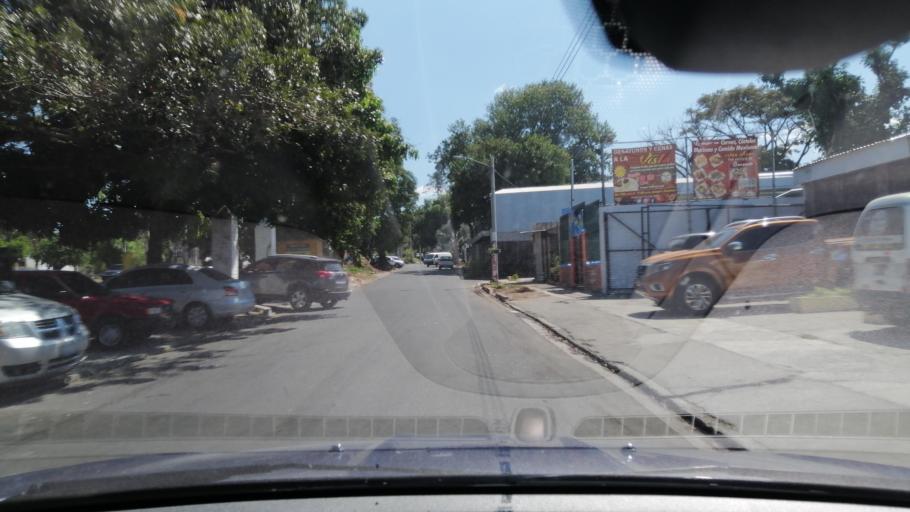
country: SV
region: Santa Ana
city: Santa Ana
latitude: 13.9716
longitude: -89.5638
